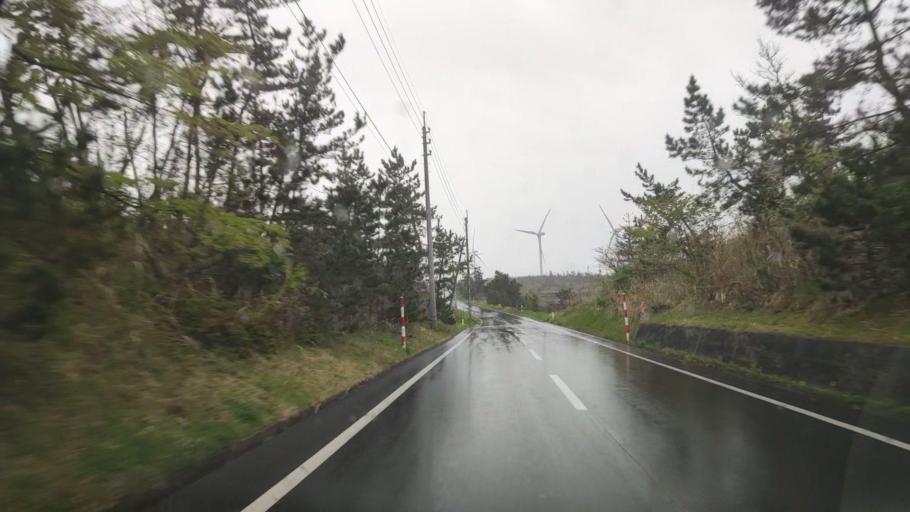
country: JP
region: Akita
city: Noshiromachi
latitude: 40.0788
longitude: 139.9536
